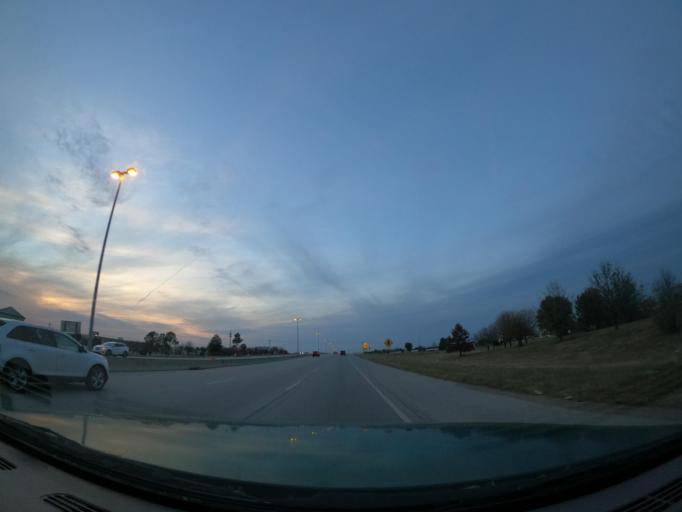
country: US
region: Oklahoma
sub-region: Tulsa County
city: Broken Arrow
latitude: 36.0783
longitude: -95.8131
